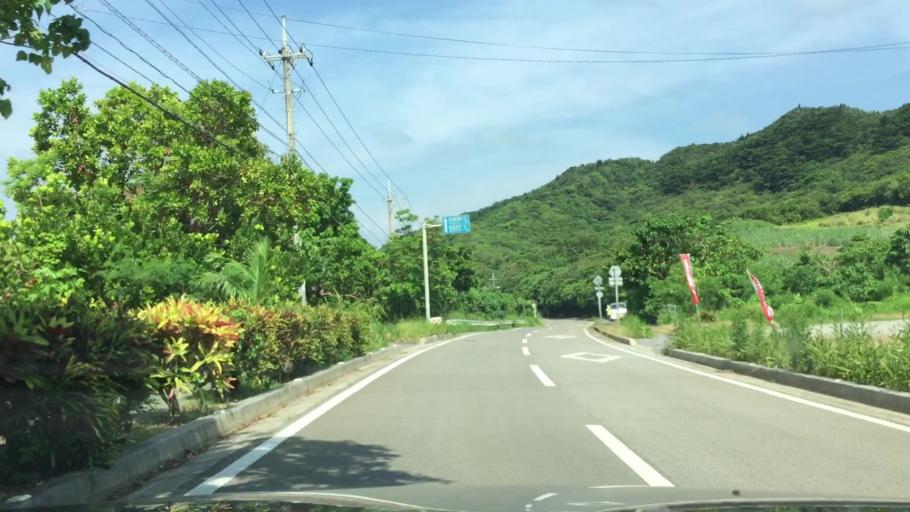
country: JP
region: Okinawa
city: Ishigaki
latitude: 24.4994
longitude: 124.2457
